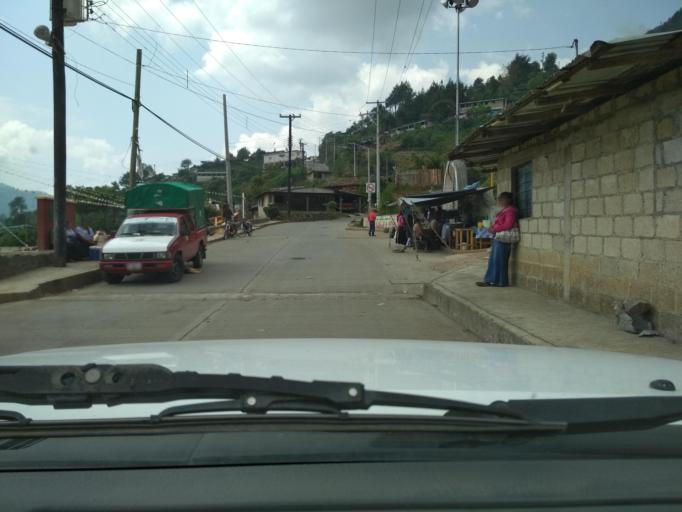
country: MX
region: Veracruz
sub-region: Camerino Z. Mendoza
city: Necoxtla
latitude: 18.7776
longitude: -97.1539
